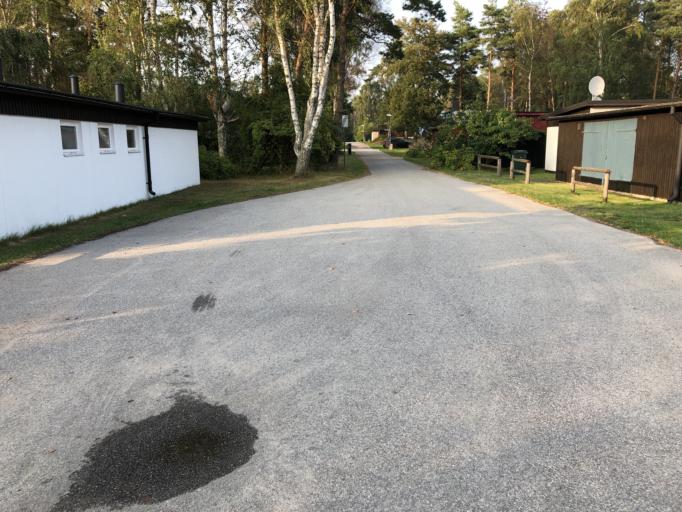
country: SE
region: Skane
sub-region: Ystads Kommun
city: Kopingebro
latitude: 55.4300
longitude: 13.9501
